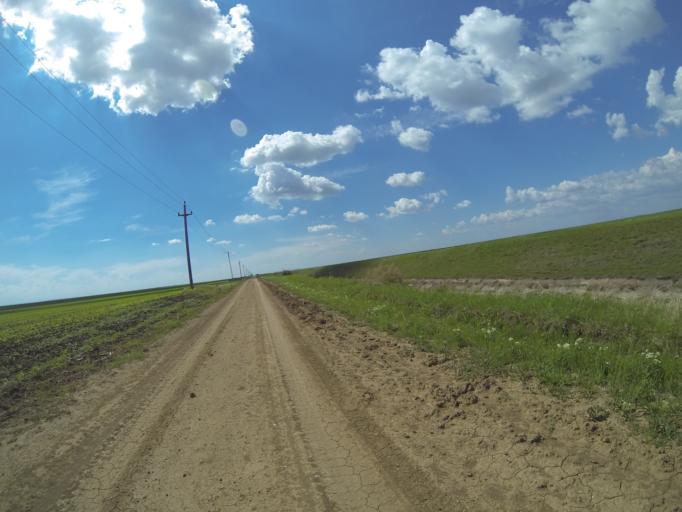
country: RO
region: Dolj
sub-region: Comuna Dranicu
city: Dranic
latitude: 44.0171
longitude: 23.7809
